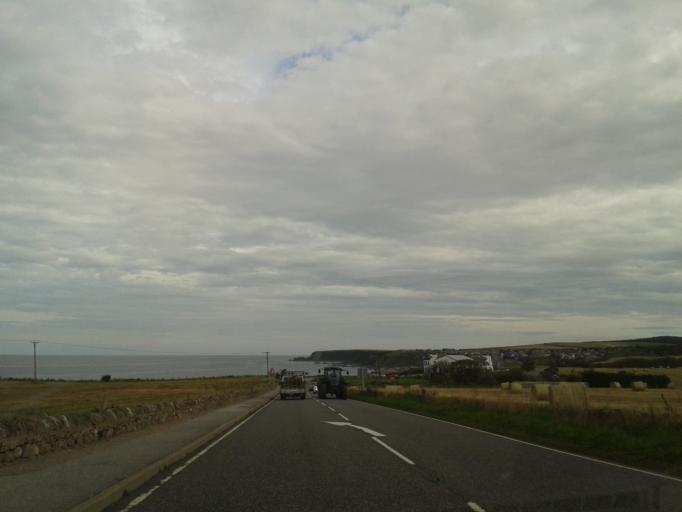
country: GB
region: Scotland
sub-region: Moray
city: Portknockie
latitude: 57.6924
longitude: -2.8447
